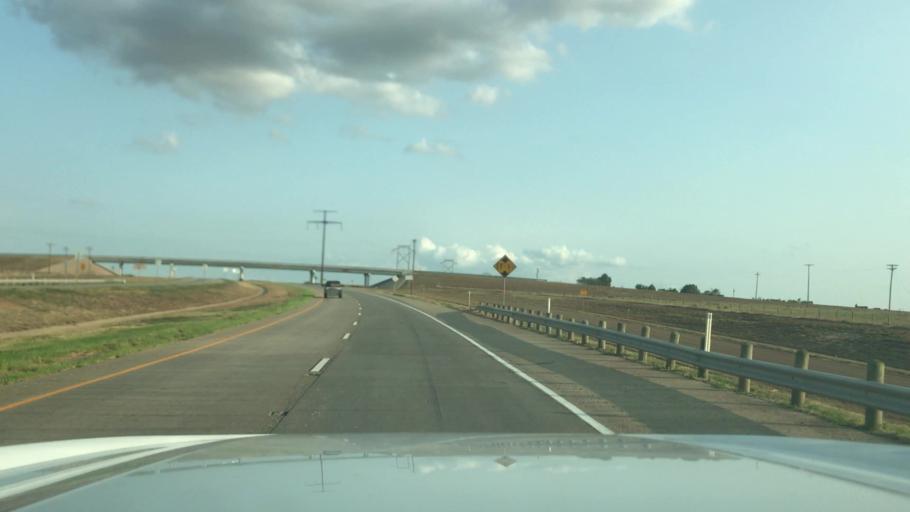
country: US
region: Texas
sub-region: Swisher County
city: Tulia
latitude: 34.5183
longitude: -101.7954
